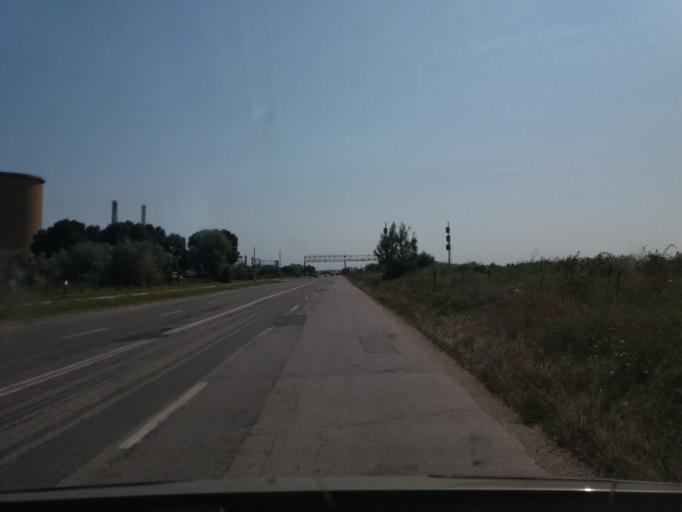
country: RO
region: Constanta
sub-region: Comuna Corbu
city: Corbu
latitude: 44.3486
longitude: 28.6458
